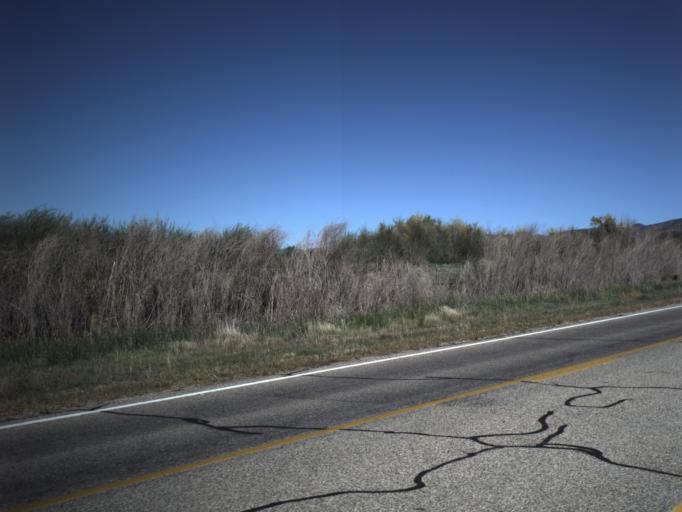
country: US
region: Utah
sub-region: Iron County
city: Parowan
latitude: 37.8386
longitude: -112.8519
